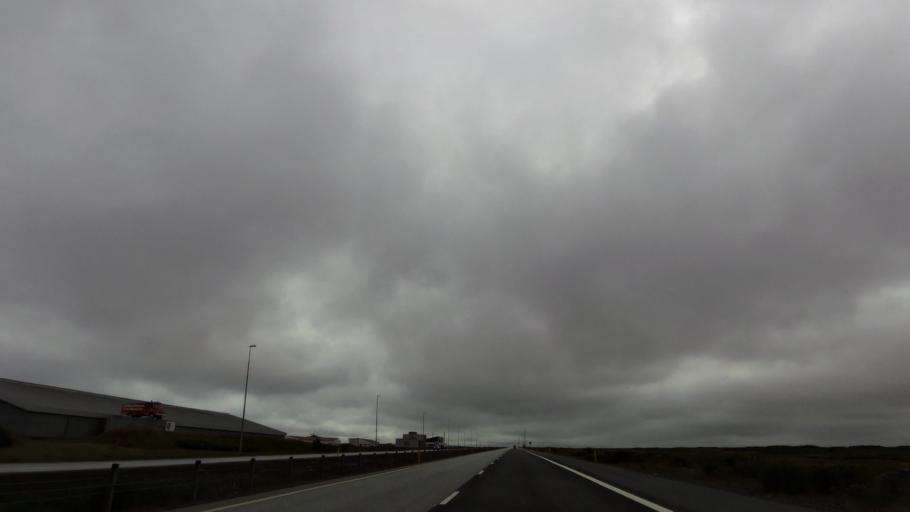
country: IS
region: Southern Peninsula
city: Reykjanesbaer
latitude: 63.9701
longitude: -22.5285
